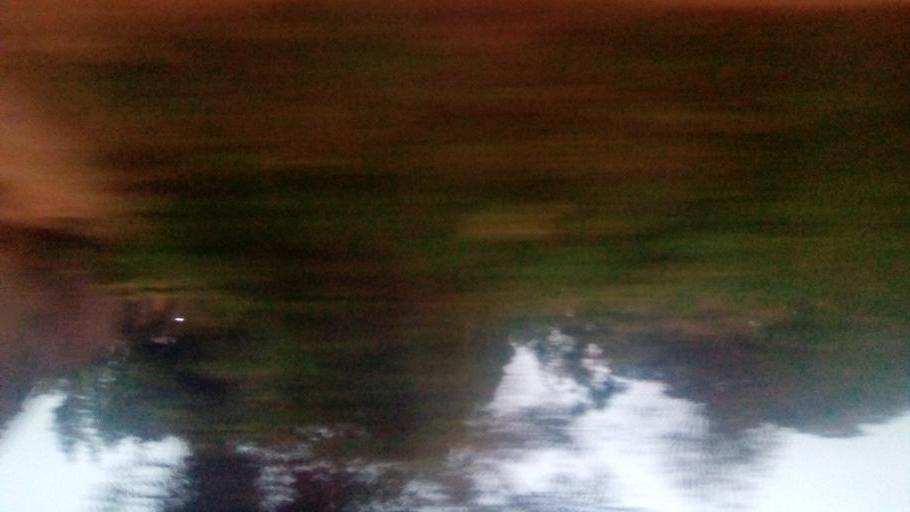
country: UG
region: Central Region
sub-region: Wakiso District
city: Wakiso
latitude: 0.4543
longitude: 32.5327
